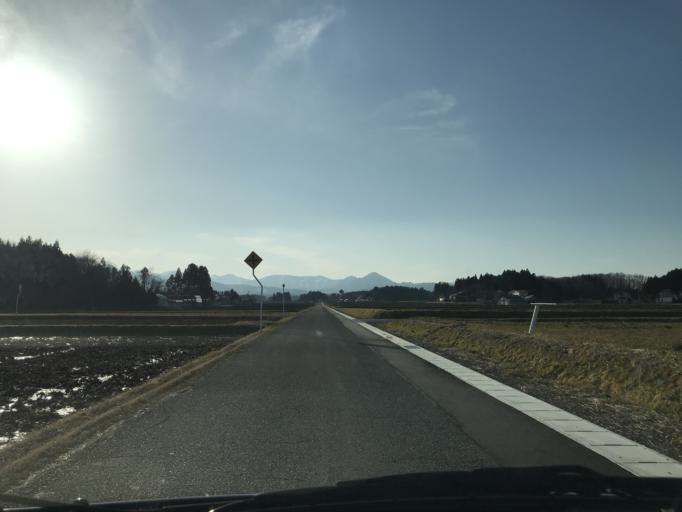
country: JP
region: Iwate
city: Kitakami
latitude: 39.2279
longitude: 141.0778
